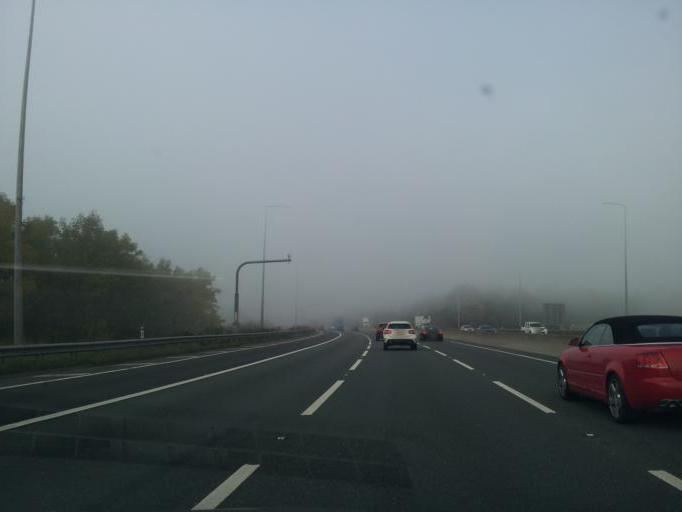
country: GB
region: England
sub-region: Kirklees
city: Cleckheaton
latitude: 53.7458
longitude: -1.7081
